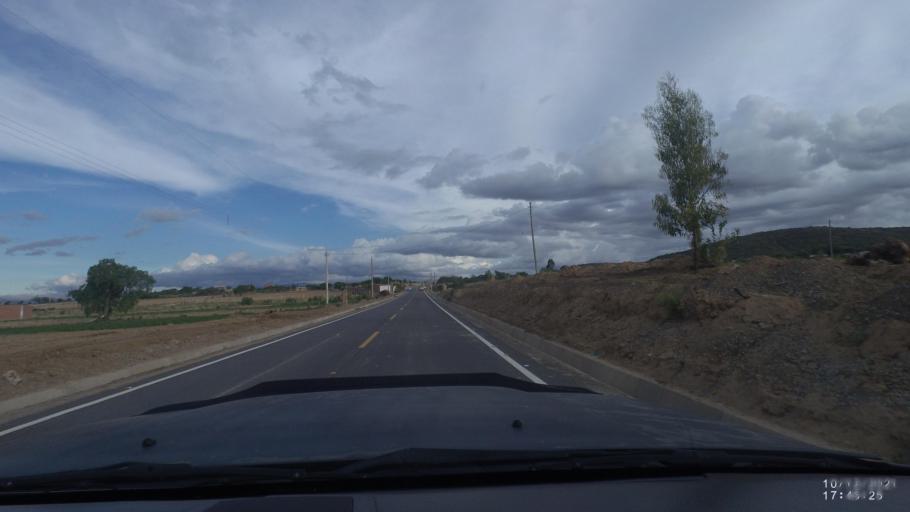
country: BO
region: Cochabamba
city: Tarata
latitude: -17.6267
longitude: -66.0028
